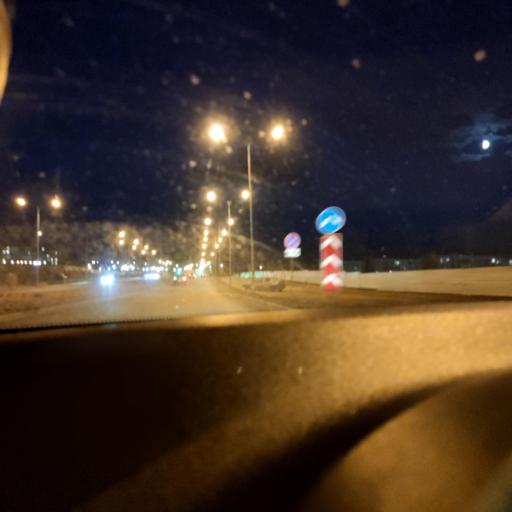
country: RU
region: Samara
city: Petra-Dubrava
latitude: 53.2982
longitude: 50.3204
